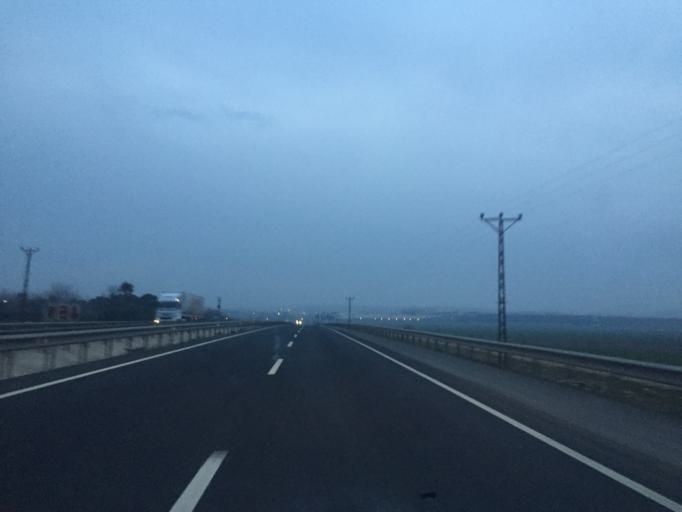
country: TR
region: Sanliurfa
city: Camlidere
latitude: 37.1524
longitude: 39.0741
